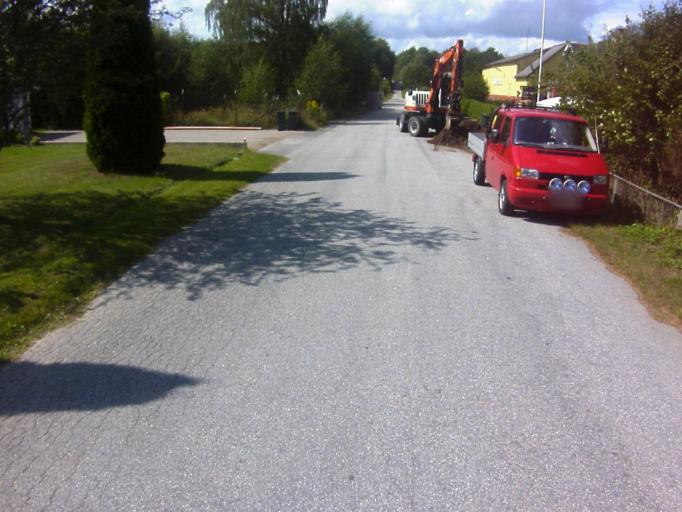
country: SE
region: Blekinge
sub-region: Karlshamns Kommun
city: Morrum
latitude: 56.1612
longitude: 14.6767
